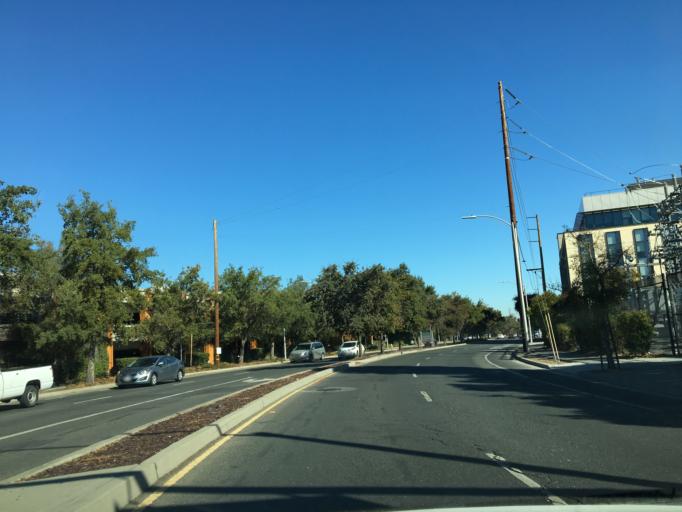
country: US
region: California
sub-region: San Mateo County
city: Menlo Park
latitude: 37.4410
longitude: -122.1704
